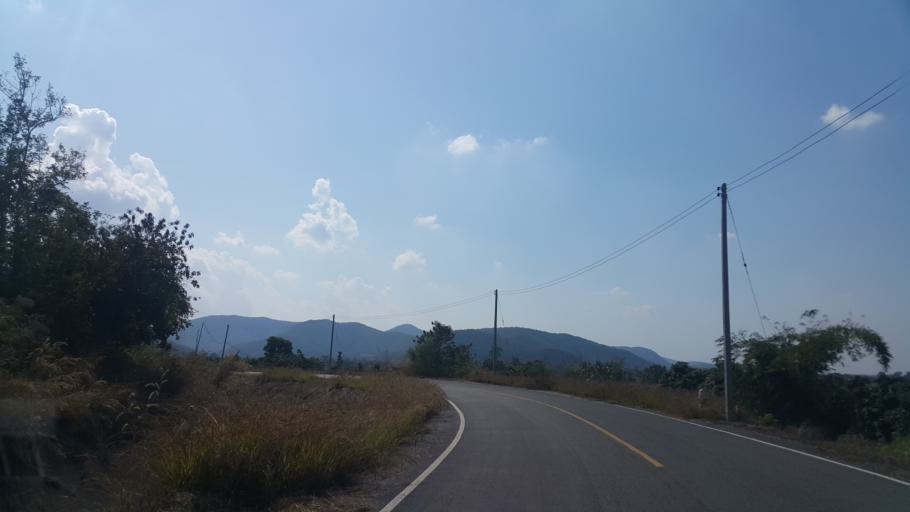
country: TH
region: Lamphun
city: Ban Thi
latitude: 18.6382
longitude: 99.1609
